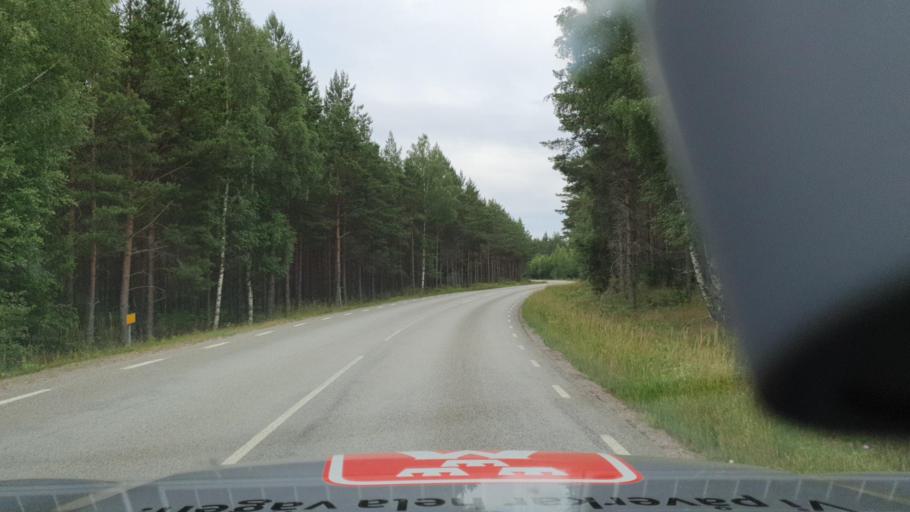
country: SE
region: Kalmar
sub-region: Nybro Kommun
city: Nybro
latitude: 56.6696
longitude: 15.9932
